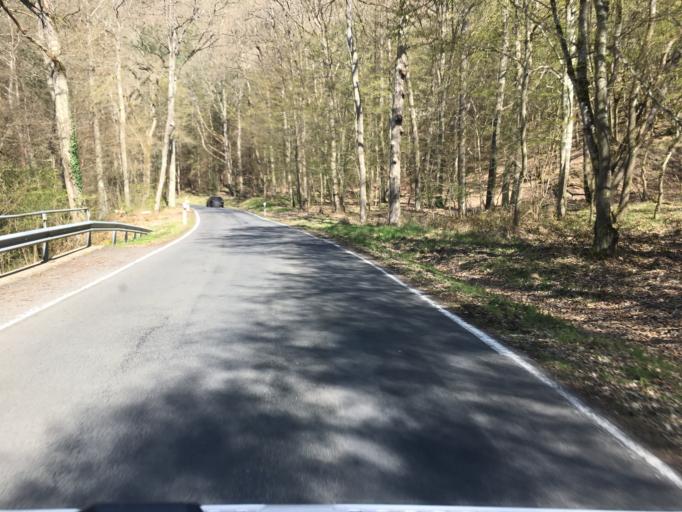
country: DE
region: Rheinland-Pfalz
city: Lind
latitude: 50.5153
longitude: 6.9576
